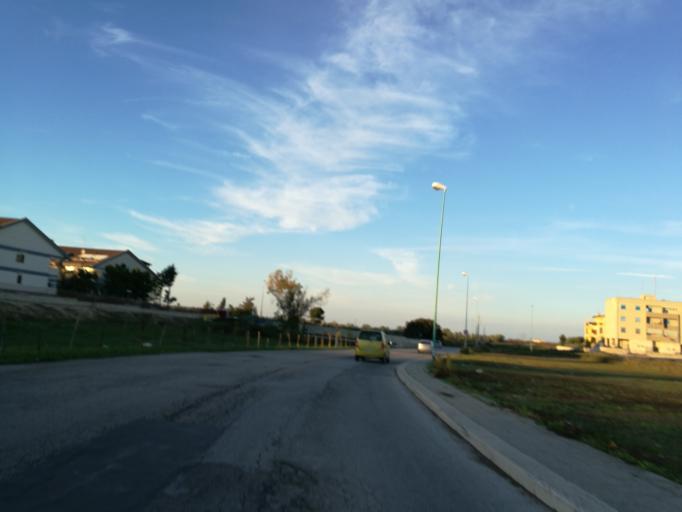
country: IT
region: Apulia
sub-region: Provincia di Bari
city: Adelfia
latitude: 41.0067
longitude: 16.8742
